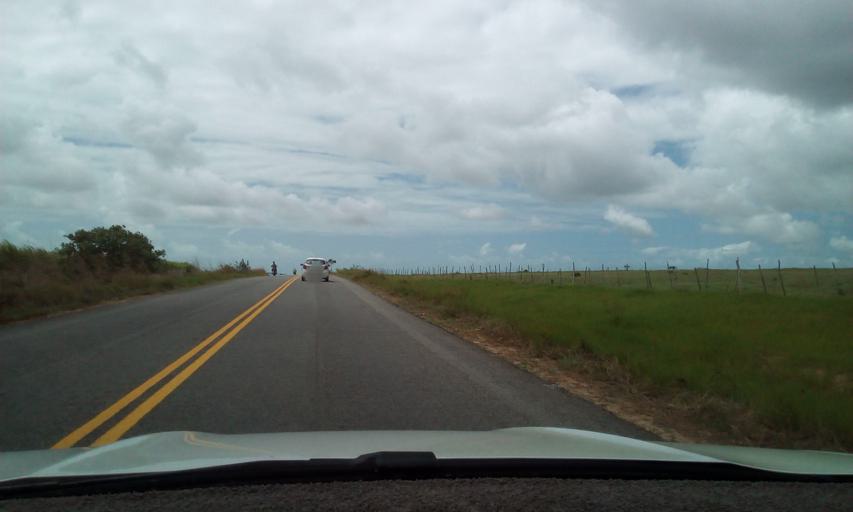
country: BR
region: Paraiba
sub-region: Rio Tinto
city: Rio Tinto
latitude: -6.7740
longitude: -35.0421
